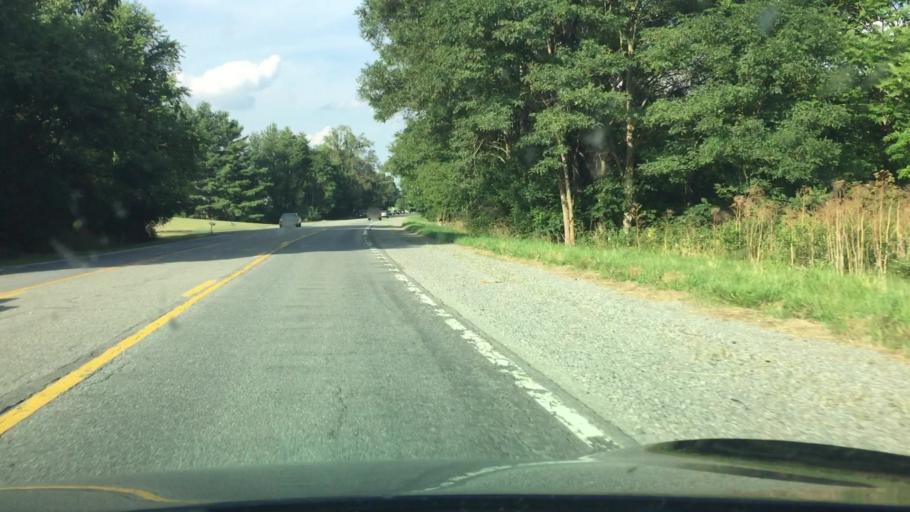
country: US
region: Virginia
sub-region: Pulaski County
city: Dublin
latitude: 37.1171
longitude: -80.6668
